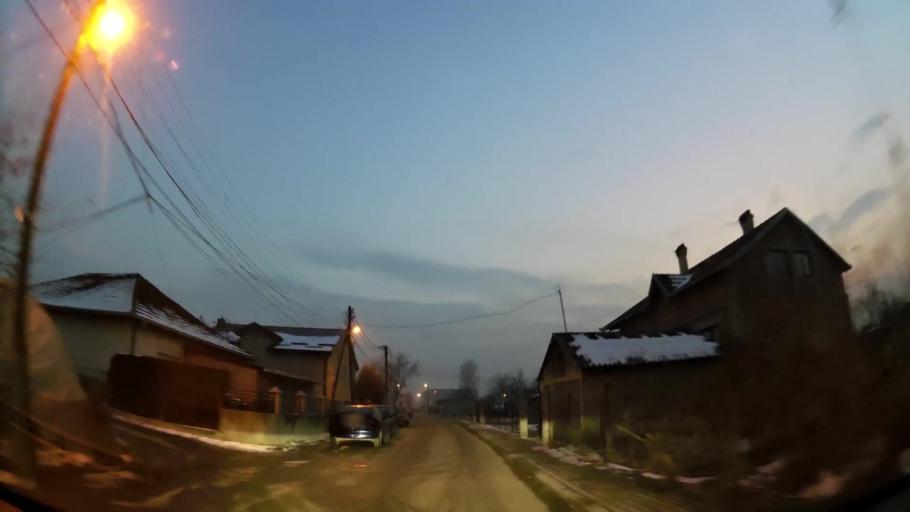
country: MK
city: Creshevo
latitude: 42.0003
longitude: 21.5174
